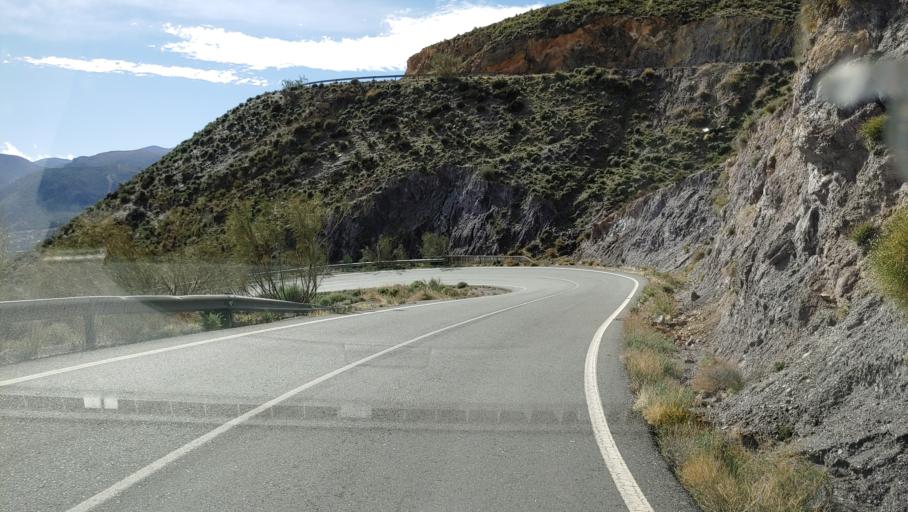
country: ES
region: Andalusia
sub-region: Provincia de Almeria
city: Canjayar
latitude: 37.0252
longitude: -2.7294
